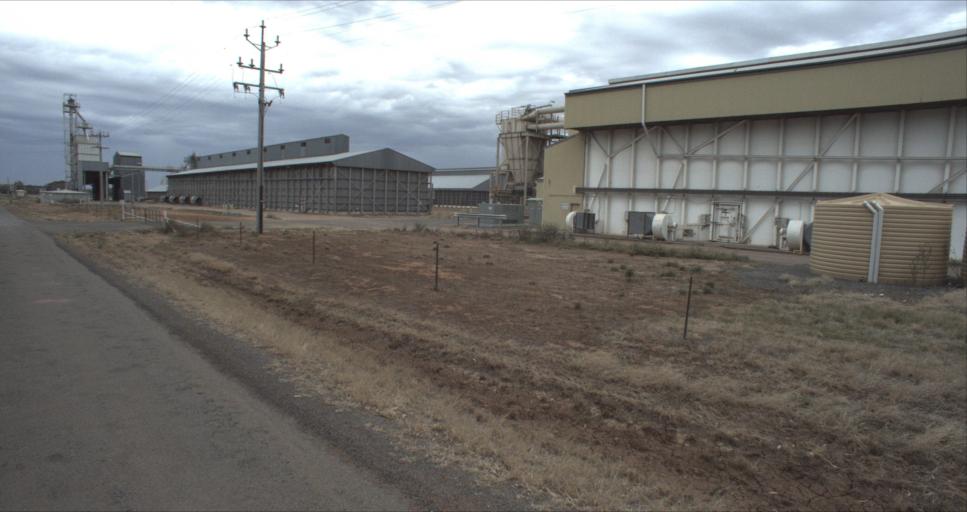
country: AU
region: New South Wales
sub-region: Leeton
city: Leeton
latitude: -34.4285
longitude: 146.3064
